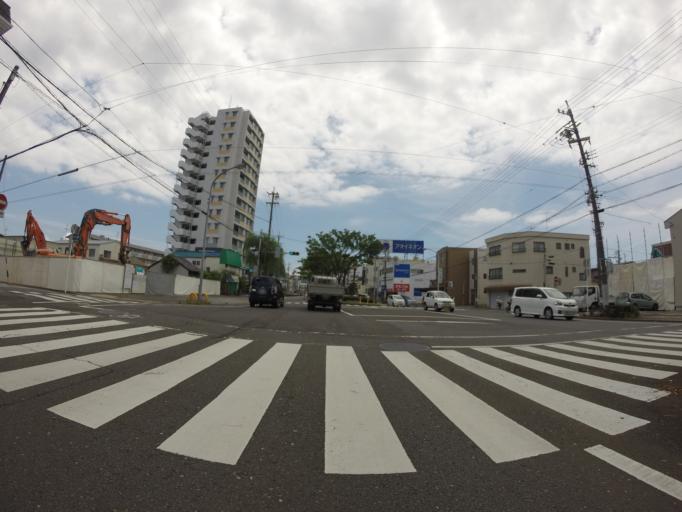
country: JP
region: Shizuoka
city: Shizuoka-shi
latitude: 34.9723
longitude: 138.3957
